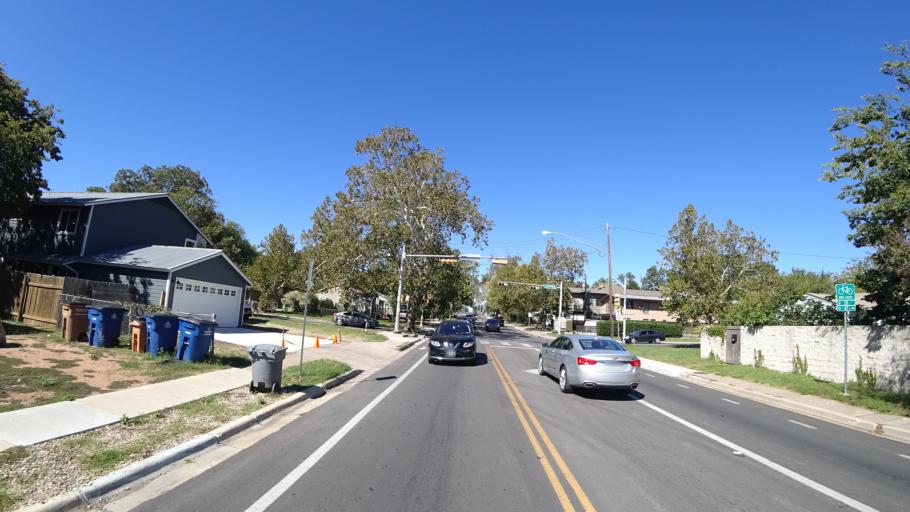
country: US
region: Texas
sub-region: Travis County
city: Austin
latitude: 30.3198
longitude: -97.7267
